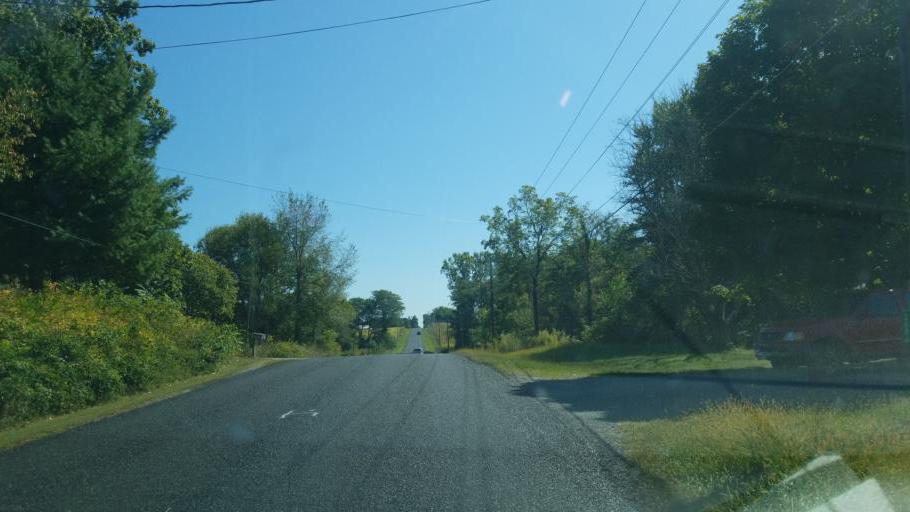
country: US
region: Ohio
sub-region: Logan County
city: Bellefontaine
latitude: 40.3253
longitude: -83.7413
